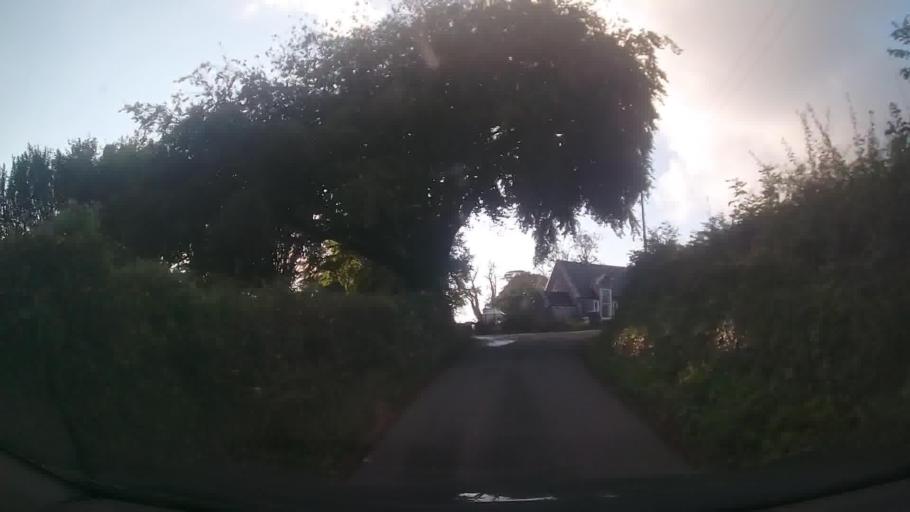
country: GB
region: Wales
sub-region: Pembrokeshire
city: Saundersfoot
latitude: 51.7397
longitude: -4.6611
